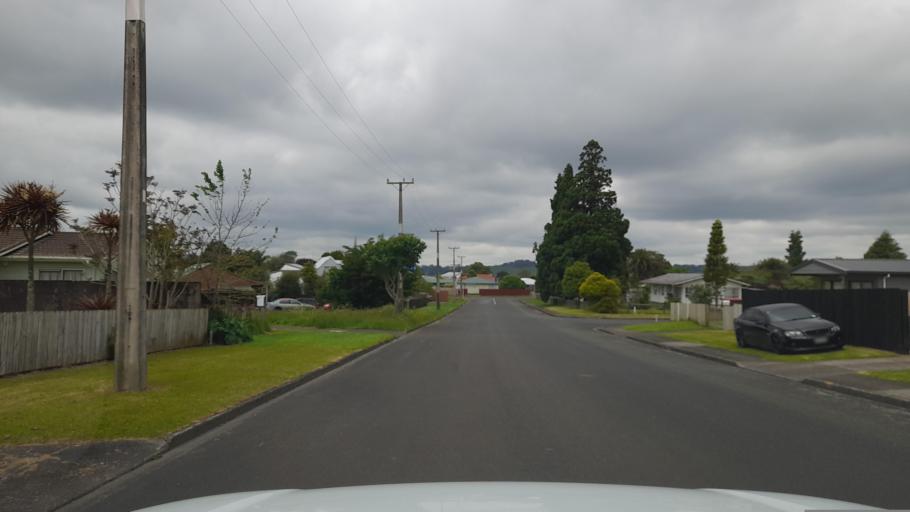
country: NZ
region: Northland
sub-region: Far North District
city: Waimate North
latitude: -35.4085
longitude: 173.7894
